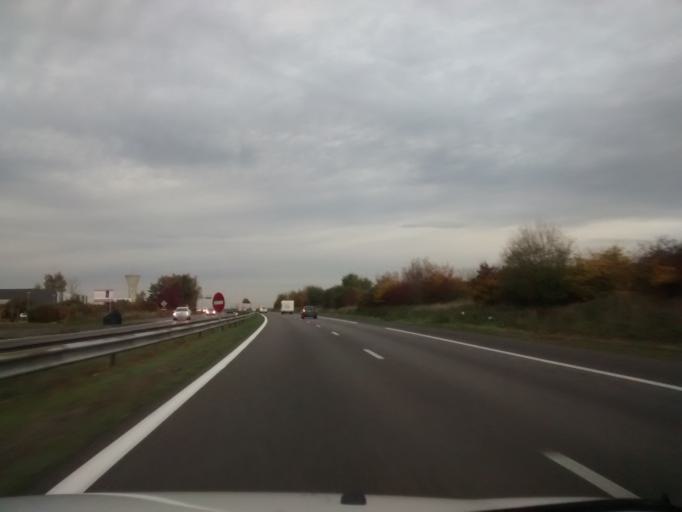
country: FR
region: Brittany
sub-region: Departement d'Ille-et-Vilaine
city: Pleumeleuc
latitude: 48.1815
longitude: -1.9312
